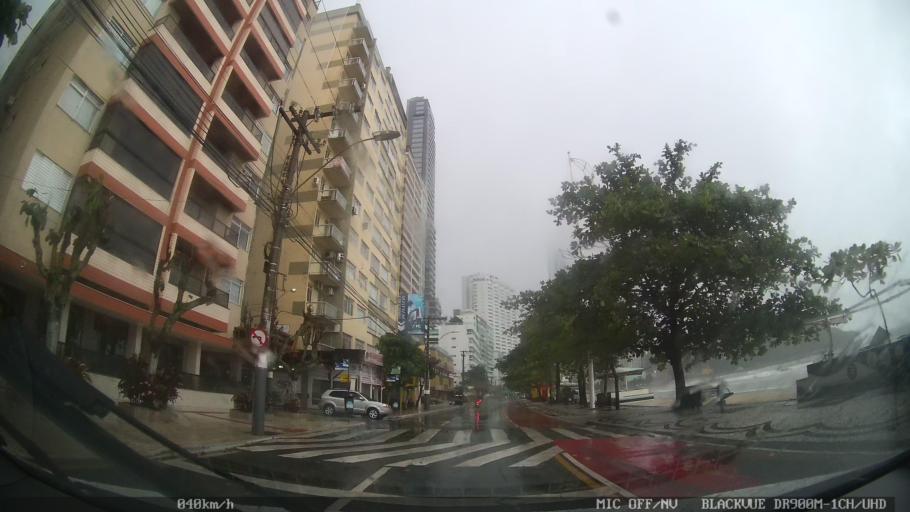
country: BR
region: Santa Catarina
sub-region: Balneario Camboriu
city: Balneario Camboriu
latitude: -26.9757
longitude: -48.6353
